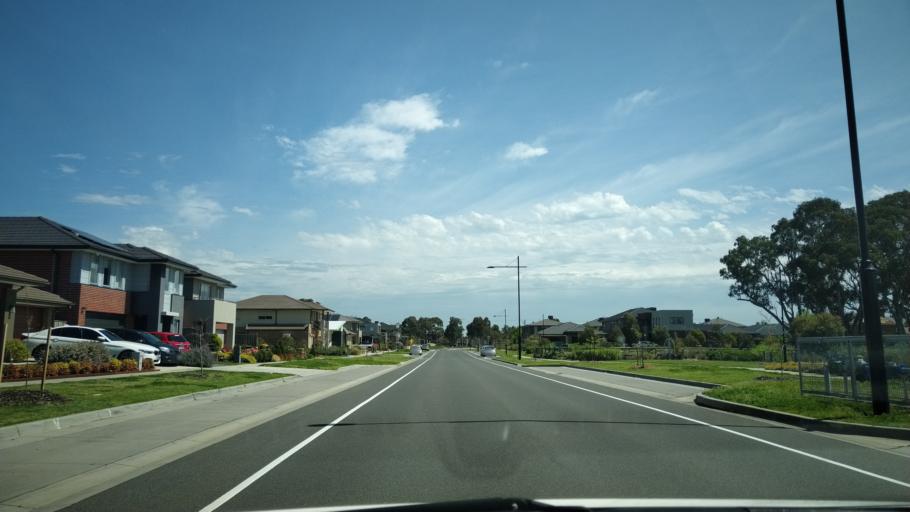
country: AU
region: Victoria
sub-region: Greater Dandenong
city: Keysborough
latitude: -38.0044
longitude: 145.1638
